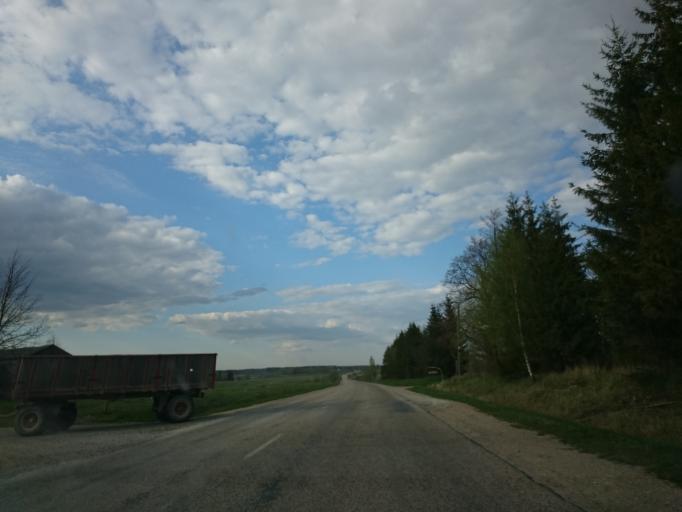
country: LV
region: Aizpute
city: Aizpute
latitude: 56.7409
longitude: 21.6092
